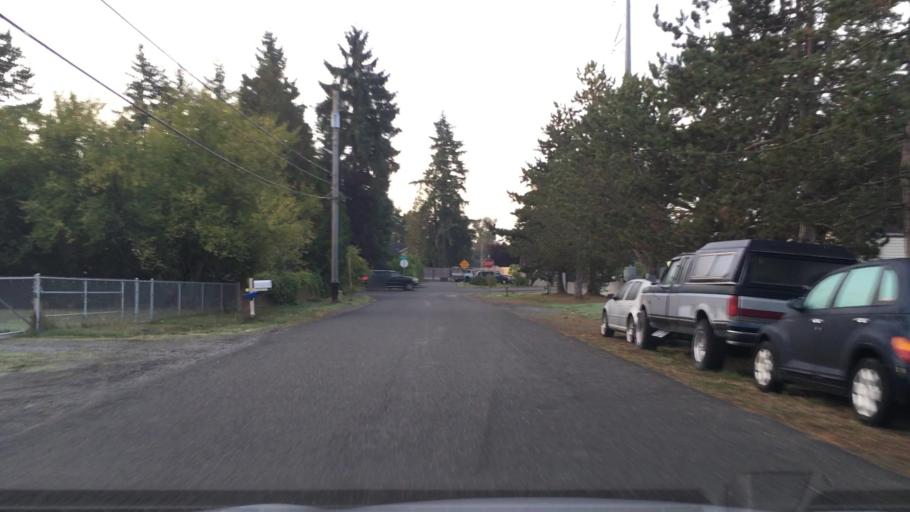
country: US
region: Washington
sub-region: Pierce County
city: Midland
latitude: 47.1811
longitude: -122.4024
